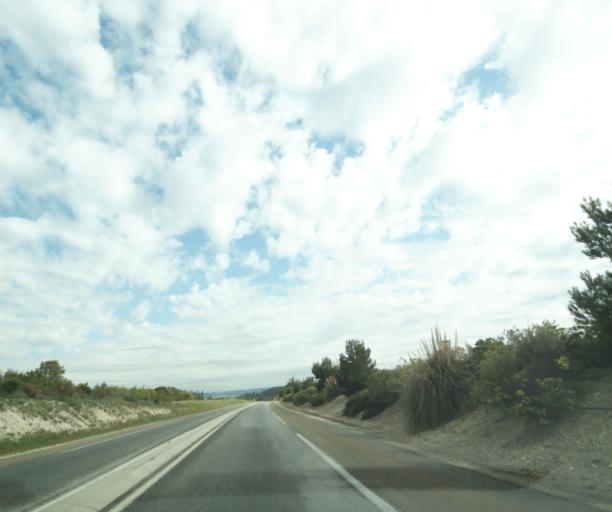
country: FR
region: Provence-Alpes-Cote d'Azur
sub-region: Departement des Bouches-du-Rhone
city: Cabries
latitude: 43.4673
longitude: 5.3541
